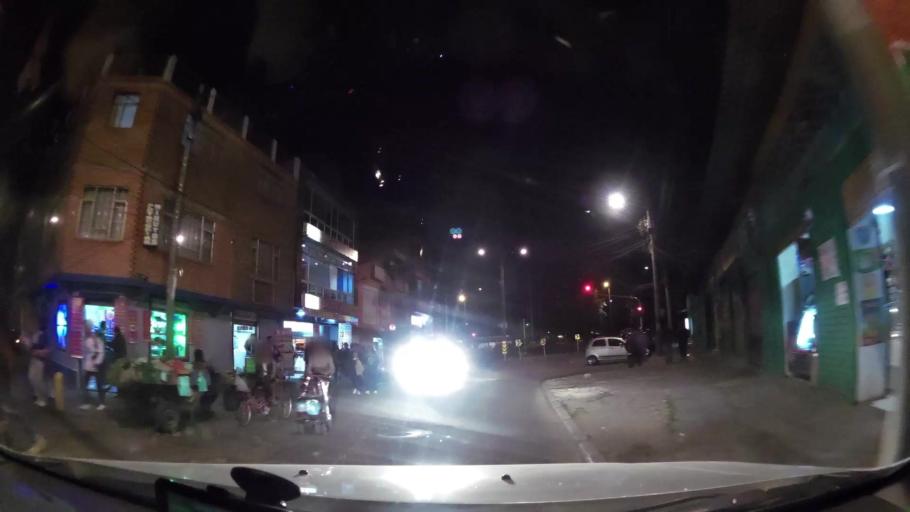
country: CO
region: Bogota D.C.
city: Bogota
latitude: 4.5700
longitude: -74.1296
